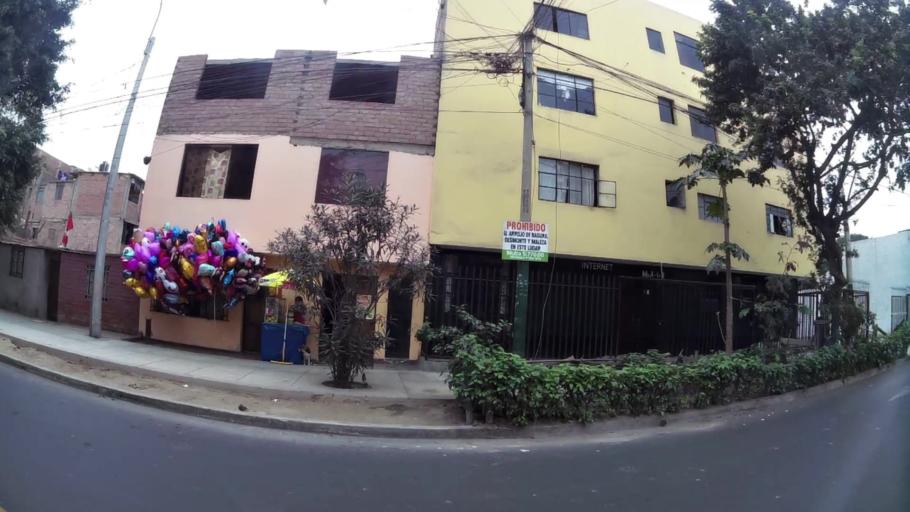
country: PE
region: Lima
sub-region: Lima
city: Surco
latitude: -12.1482
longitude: -77.0143
